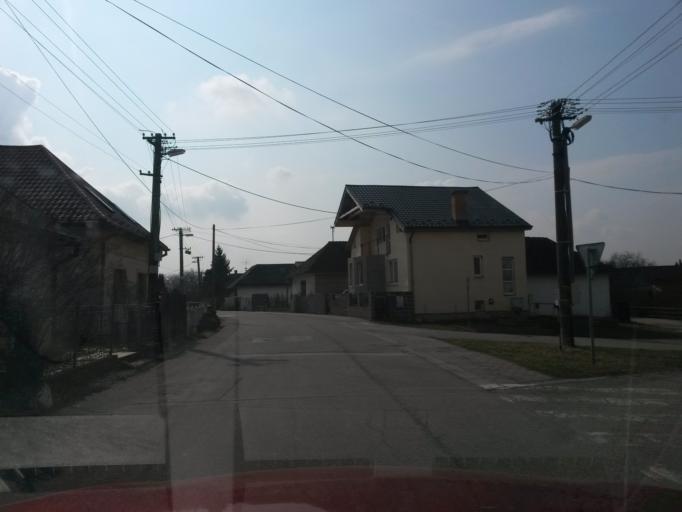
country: SK
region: Kosicky
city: Kosice
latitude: 48.6325
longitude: 21.1675
